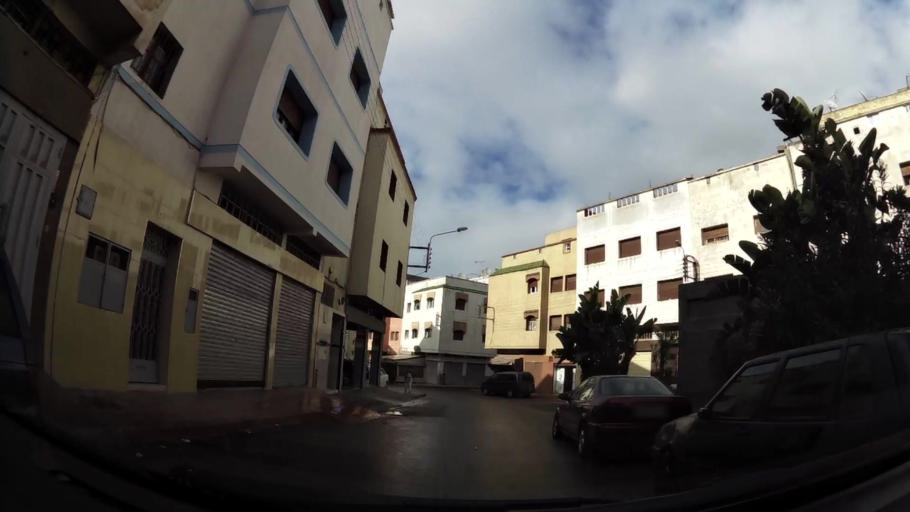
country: MA
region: Grand Casablanca
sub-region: Casablanca
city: Casablanca
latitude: 33.5457
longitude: -7.5970
